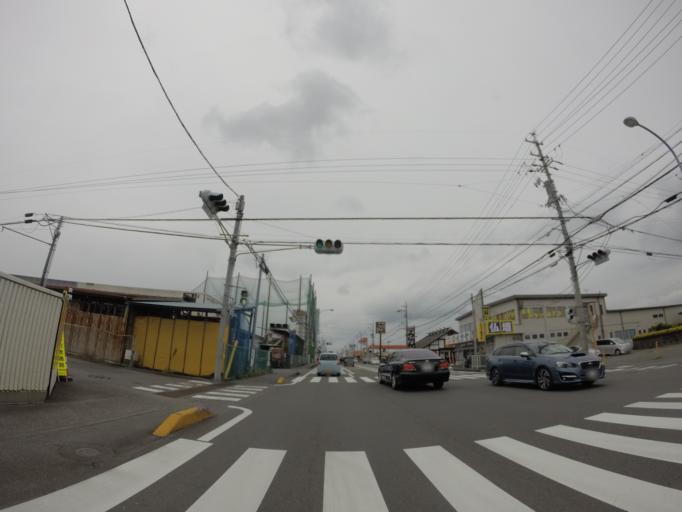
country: JP
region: Shizuoka
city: Fujieda
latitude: 34.8598
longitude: 138.2757
